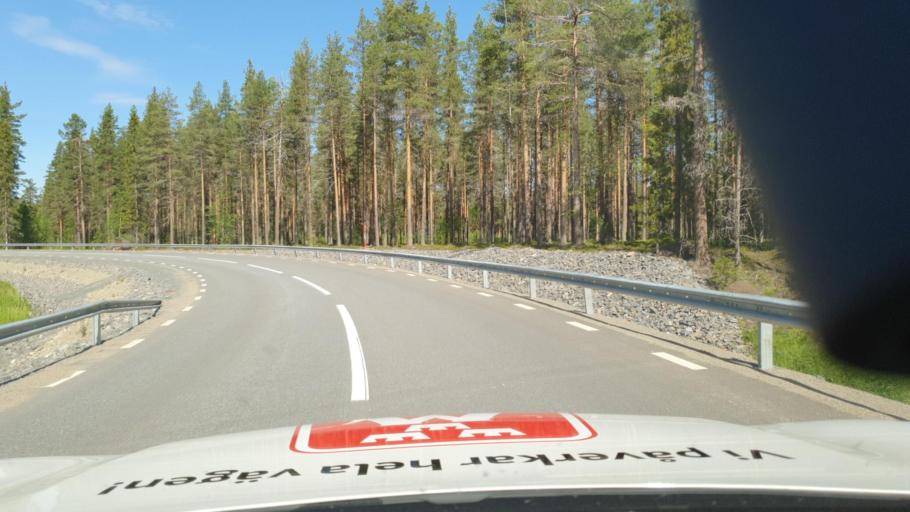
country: SE
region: Vaesterbotten
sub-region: Skelleftea Kommun
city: Boliden
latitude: 64.7882
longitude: 20.3446
